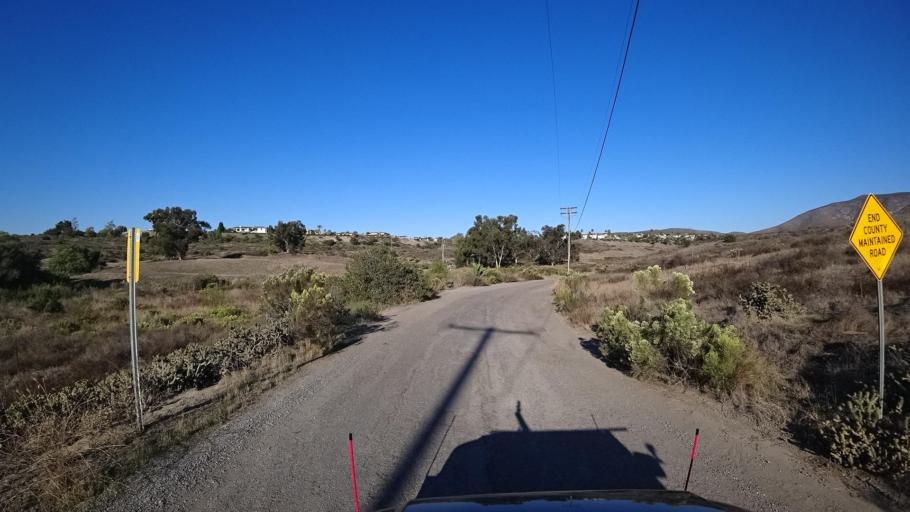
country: US
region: California
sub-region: San Diego County
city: La Presa
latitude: 32.6582
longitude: -116.9366
